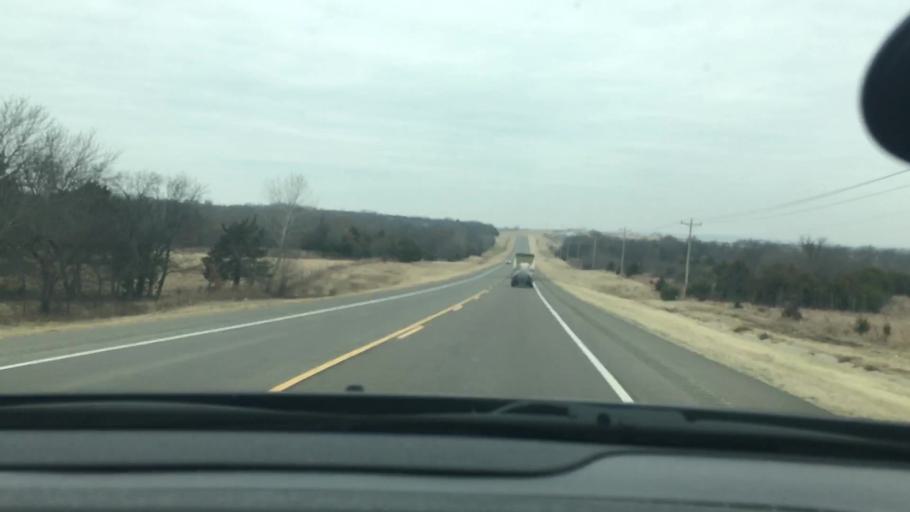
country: US
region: Oklahoma
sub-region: Murray County
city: Davis
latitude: 34.5135
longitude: -97.2009
